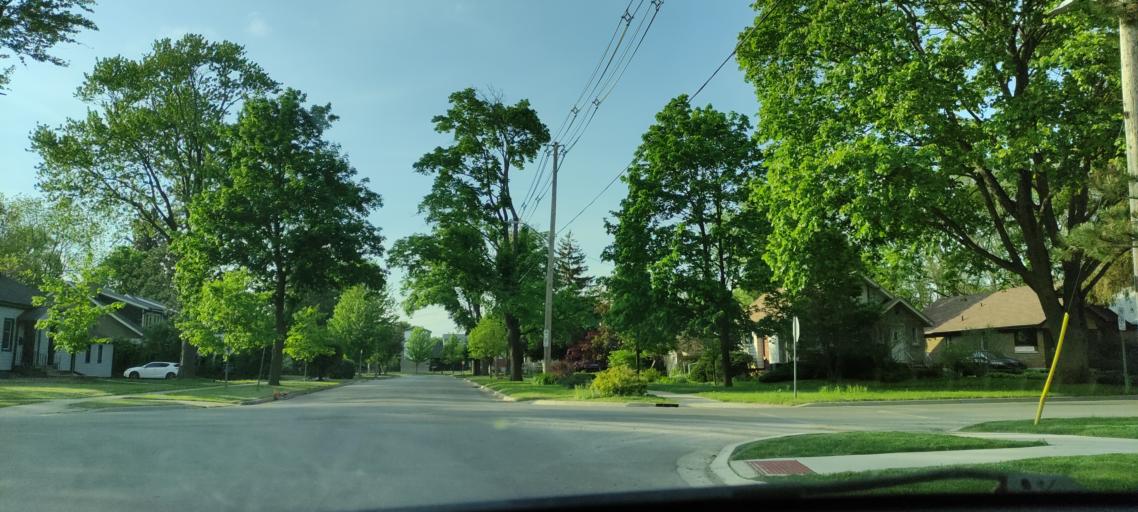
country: CA
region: Ontario
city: London
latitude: 43.0050
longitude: -81.2605
